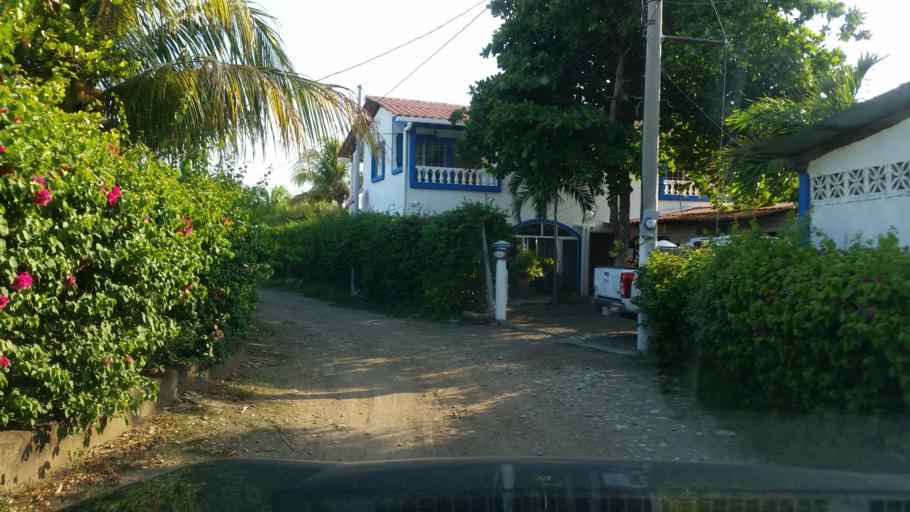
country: NI
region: Managua
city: Masachapa
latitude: 11.7619
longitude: -86.4943
